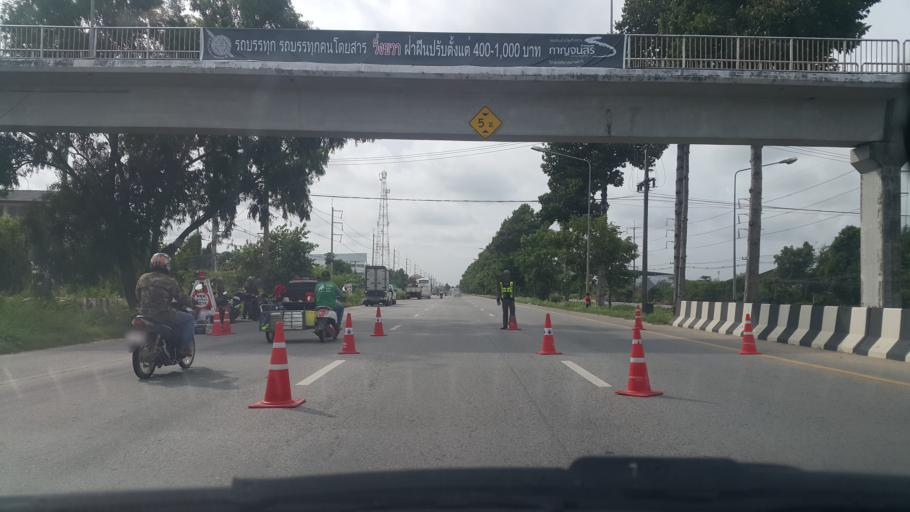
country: TH
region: Rayong
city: Rayong
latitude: 12.6744
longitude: 101.3039
